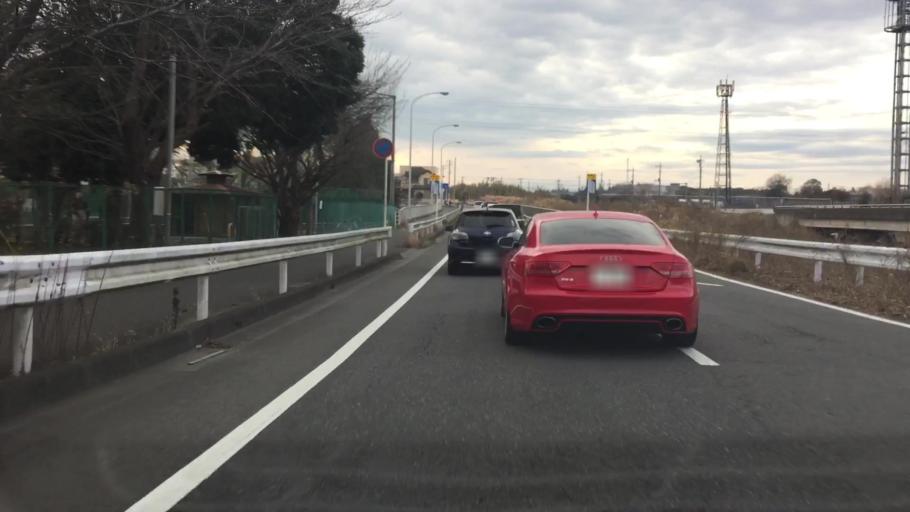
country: JP
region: Chiba
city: Shiroi
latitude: 35.7839
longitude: 140.0072
